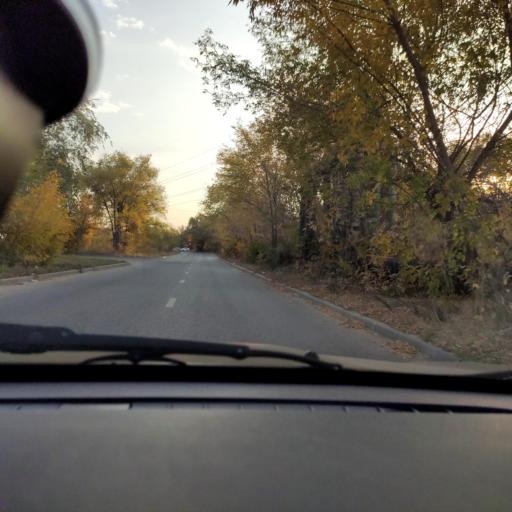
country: RU
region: Samara
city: Tol'yatti
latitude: 53.5600
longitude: 49.3213
